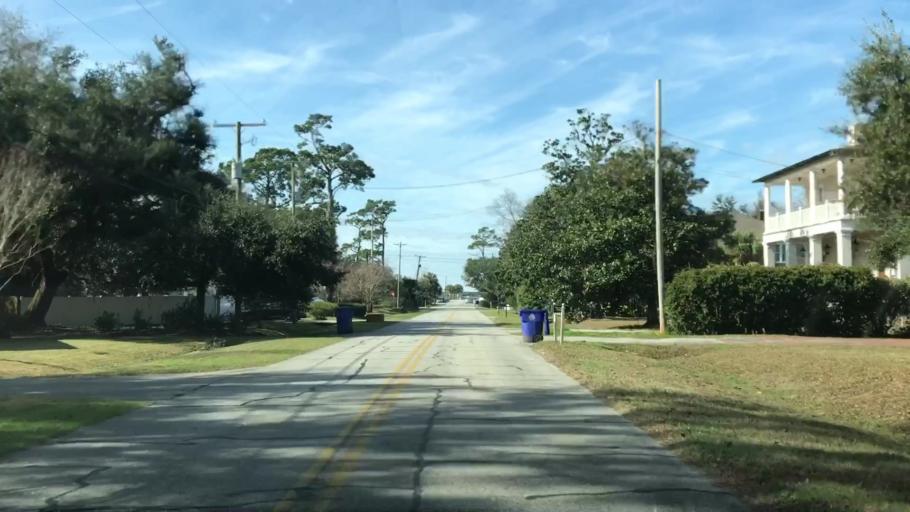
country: US
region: South Carolina
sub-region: Charleston County
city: Charleston
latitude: 32.7719
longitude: -80.0043
